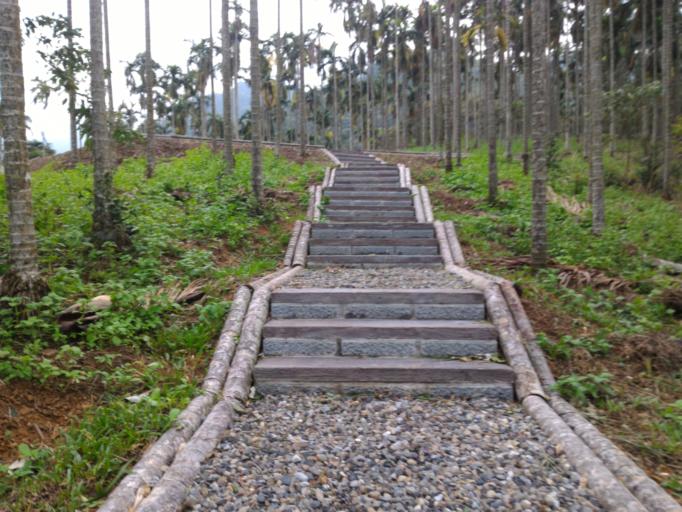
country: TW
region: Taipei
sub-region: Taipei
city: Banqiao
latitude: 24.9083
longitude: 121.4339
